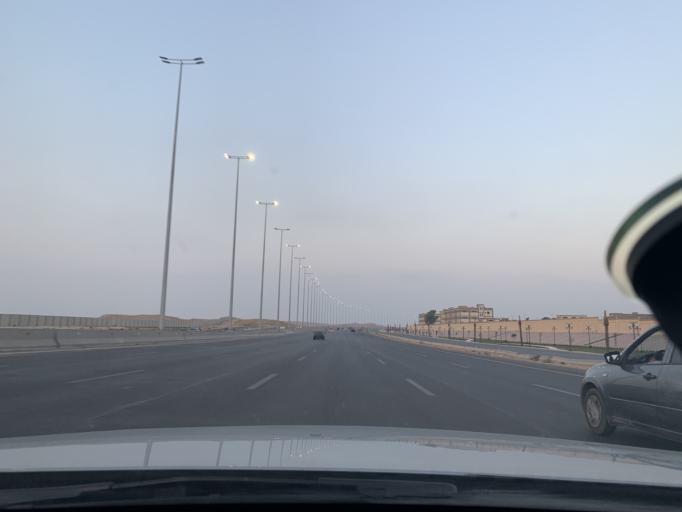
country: EG
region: Muhafazat al Qalyubiyah
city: Al Khankah
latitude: 30.0924
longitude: 31.4731
